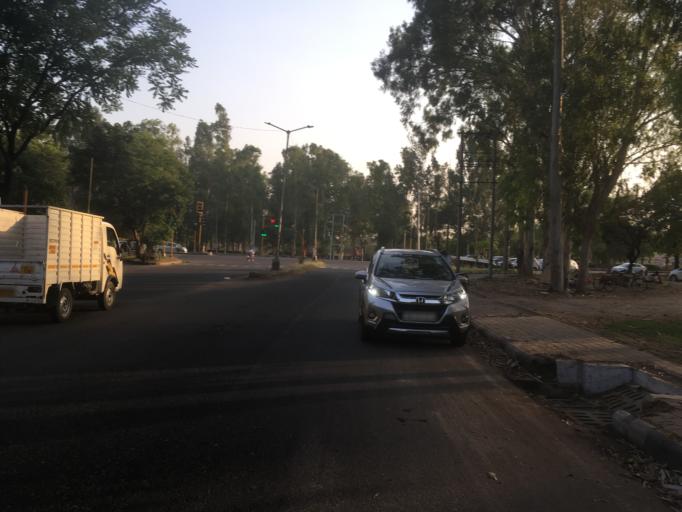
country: IN
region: Chandigarh
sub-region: Chandigarh
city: Chandigarh
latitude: 30.7098
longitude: 76.8295
